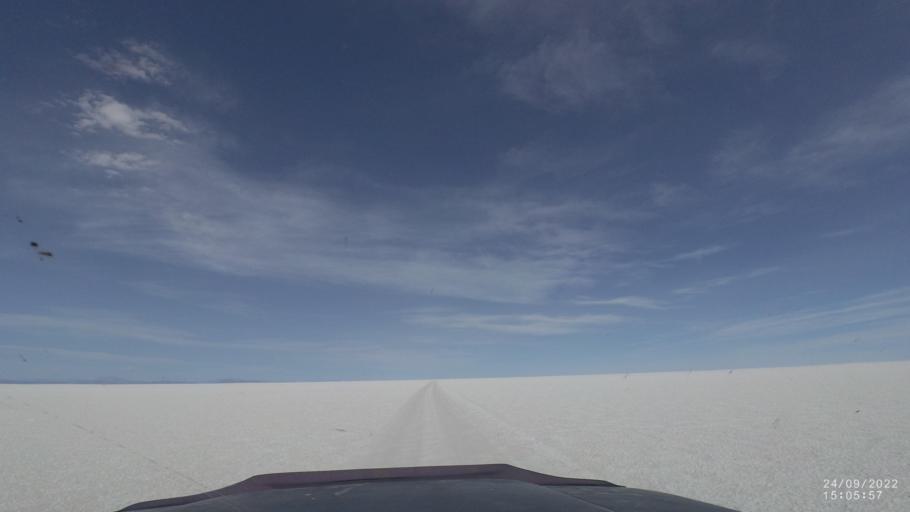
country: BO
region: Potosi
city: Colchani
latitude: -19.9097
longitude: -67.5137
